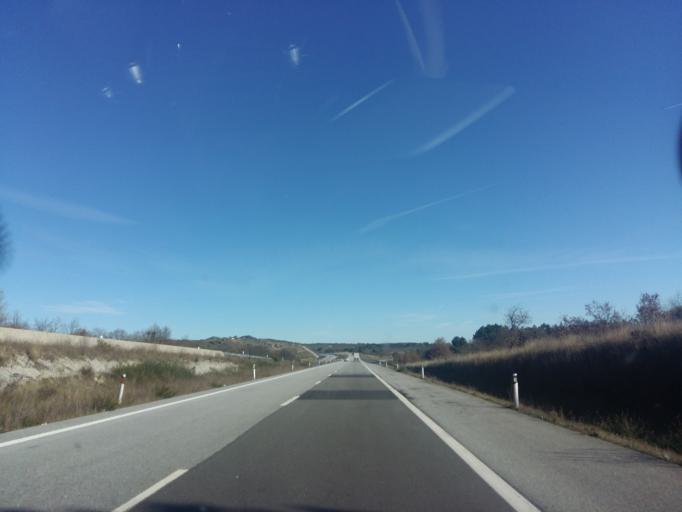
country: PT
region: Guarda
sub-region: Guarda
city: Sequeira
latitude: 40.5812
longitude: -7.1650
